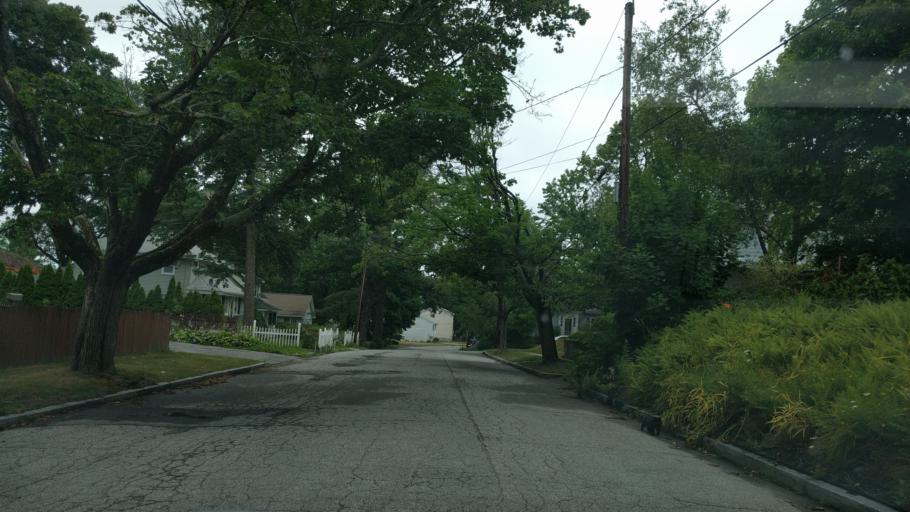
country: US
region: Massachusetts
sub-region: Worcester County
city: Worcester
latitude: 42.2918
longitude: -71.8208
